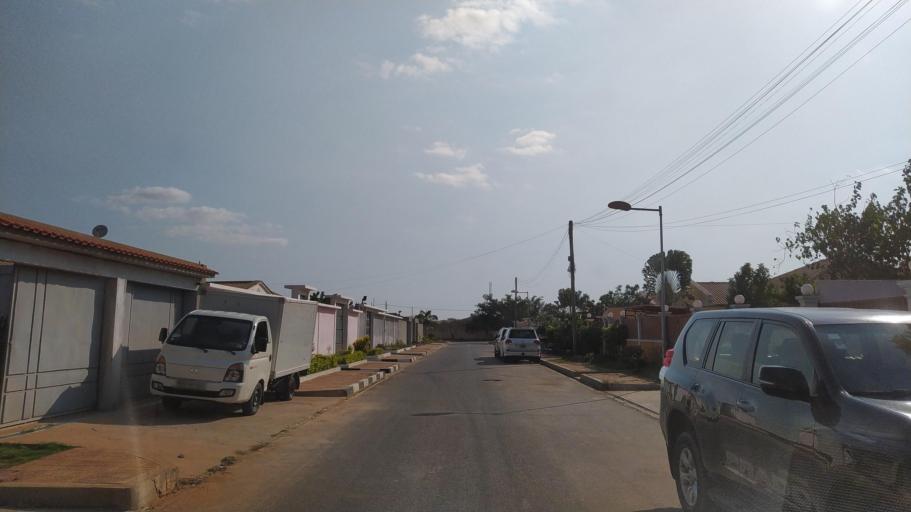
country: AO
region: Luanda
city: Luanda
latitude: -8.8930
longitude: 13.2584
